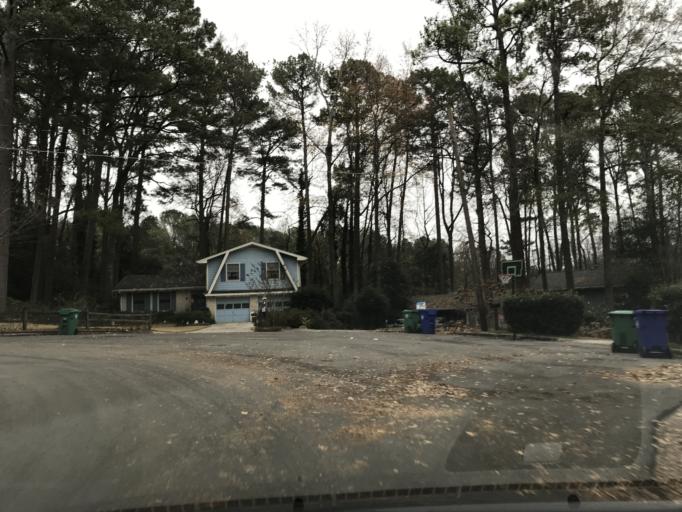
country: US
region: Georgia
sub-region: DeKalb County
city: Clarkston
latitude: 33.8151
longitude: -84.2558
